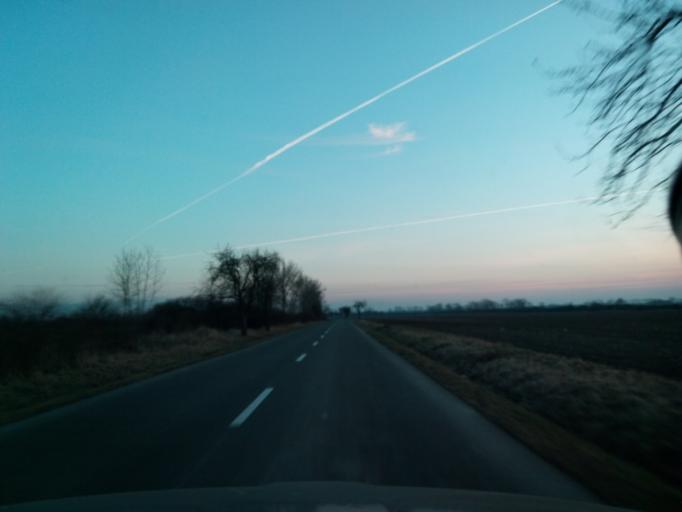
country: SK
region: Kosicky
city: Sobrance
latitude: 48.7738
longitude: 22.1269
